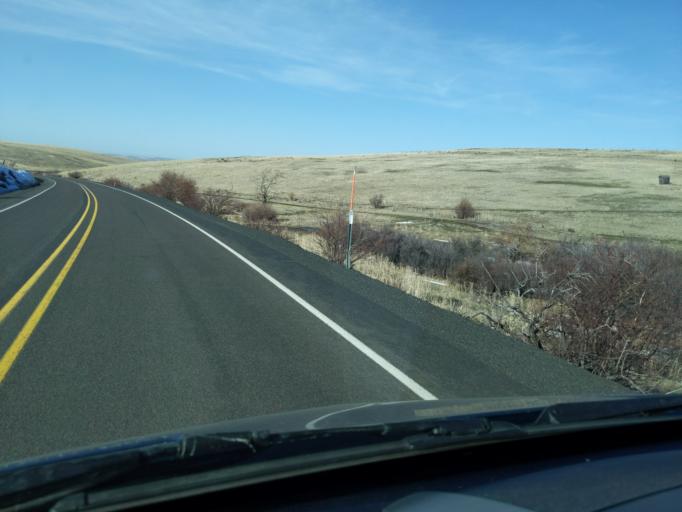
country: US
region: Oregon
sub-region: Umatilla County
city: Pilot Rock
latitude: 45.3162
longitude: -119.0020
